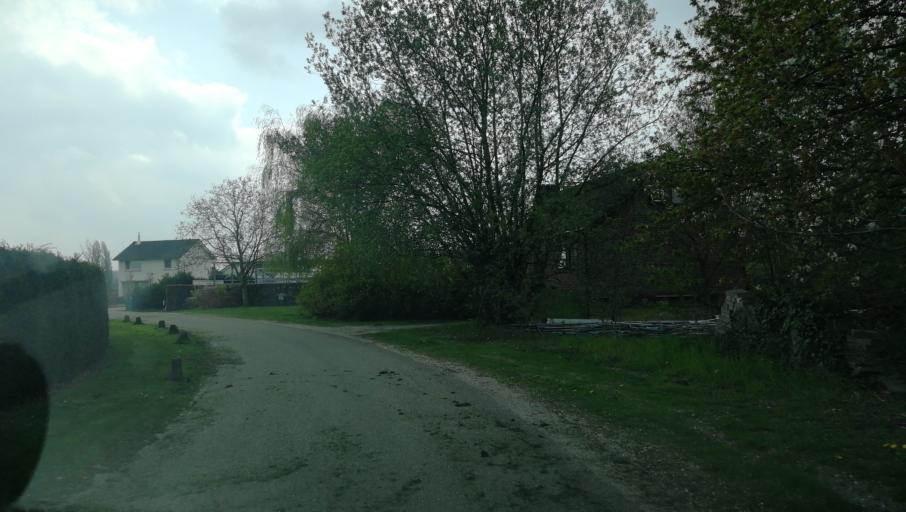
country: NL
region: Limburg
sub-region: Gemeente Venlo
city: Venlo
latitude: 51.3952
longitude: 6.2080
